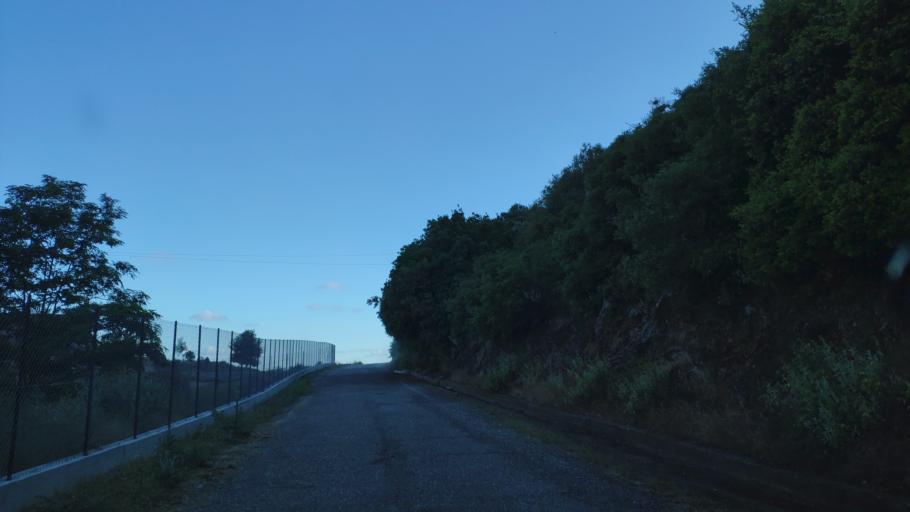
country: GR
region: West Greece
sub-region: Nomos Aitolias kai Akarnanias
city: Fitiai
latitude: 38.6497
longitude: 21.1989
